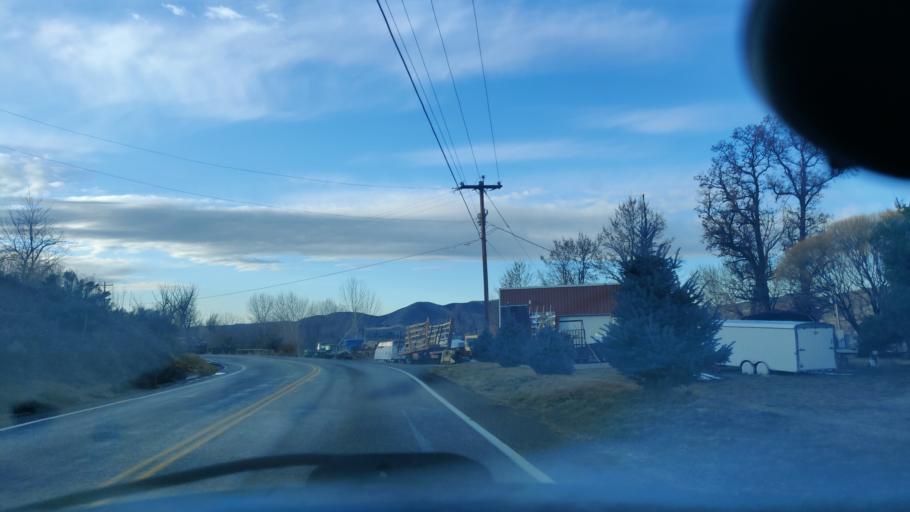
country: US
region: Idaho
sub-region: Ada County
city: Eagle
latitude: 43.7310
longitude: -116.2709
